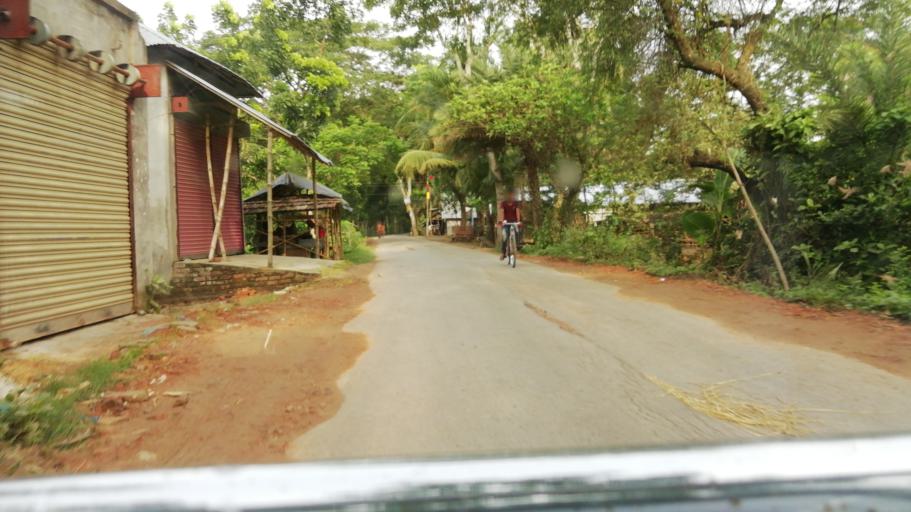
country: BD
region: Khulna
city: Bhatpara Abhaynagar
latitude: 23.0355
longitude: 89.2947
